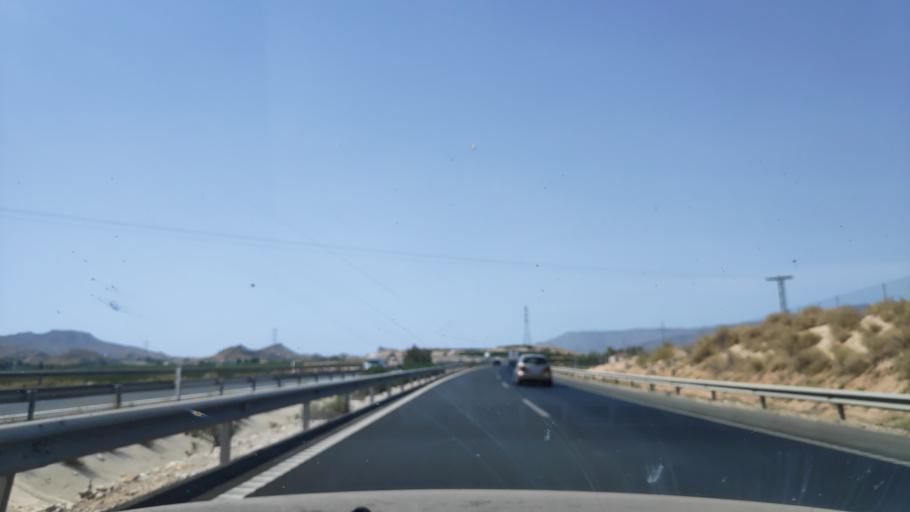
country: ES
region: Murcia
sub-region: Murcia
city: Archena
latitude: 38.1396
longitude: -1.2727
